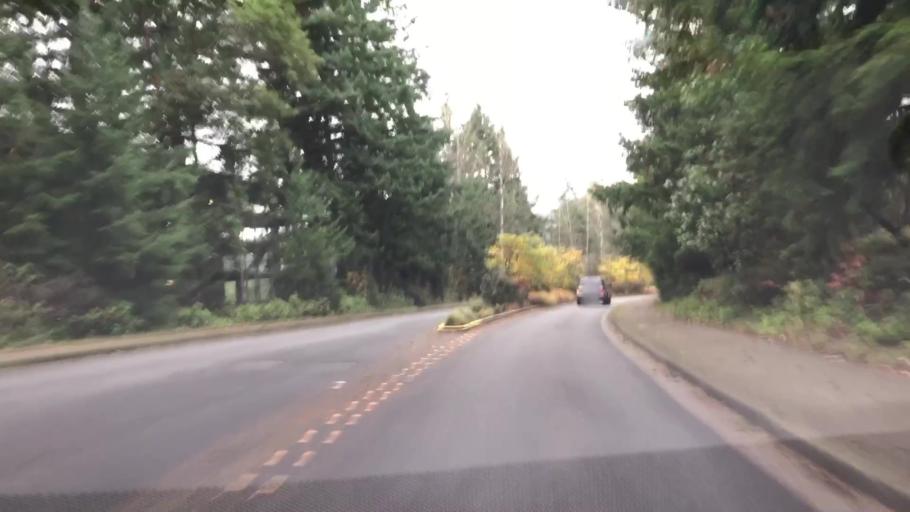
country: US
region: Washington
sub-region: King County
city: Eastgate
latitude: 47.5843
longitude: -122.1326
